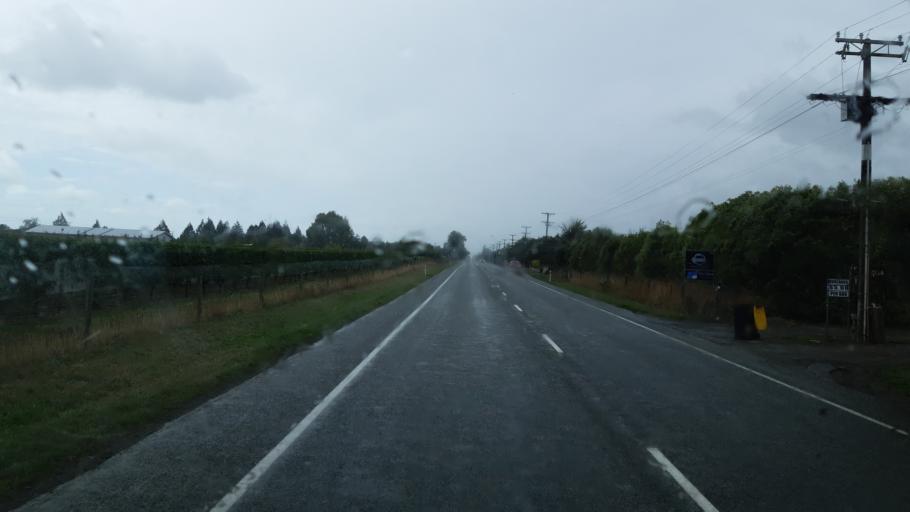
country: NZ
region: Tasman
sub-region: Tasman District
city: Brightwater
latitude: -41.3606
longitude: 173.1435
